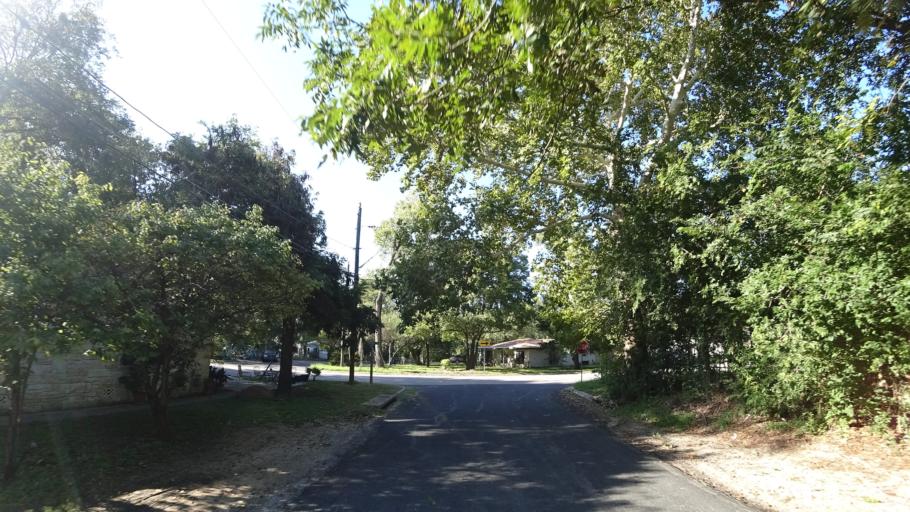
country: US
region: Texas
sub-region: Travis County
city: Wells Branch
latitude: 30.3537
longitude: -97.6959
